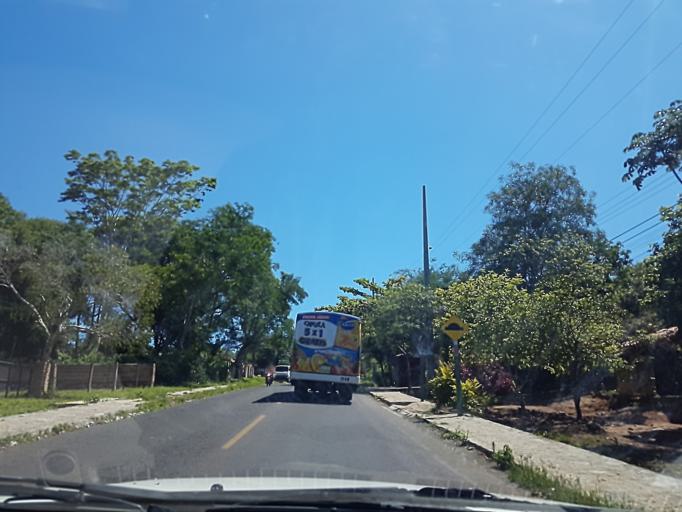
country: PY
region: Cordillera
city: Altos
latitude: -25.2589
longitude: -57.2473
